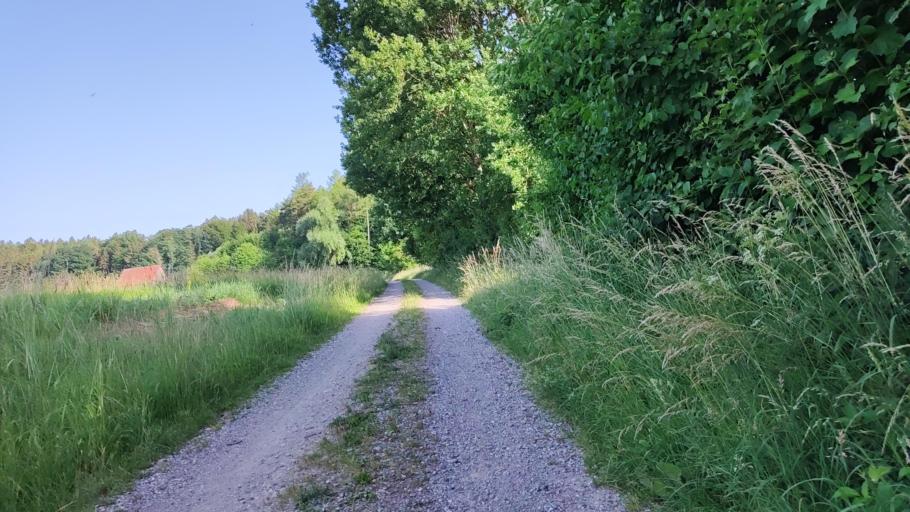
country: DE
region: Bavaria
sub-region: Swabia
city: Altenmunster
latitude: 48.4763
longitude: 10.5822
